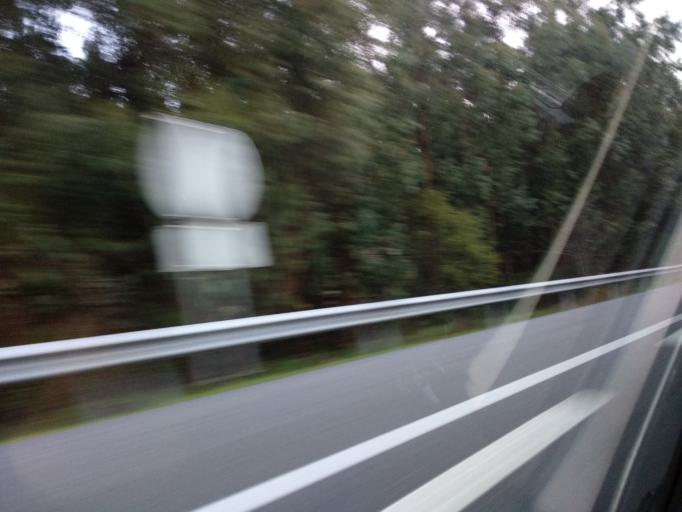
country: PT
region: Braga
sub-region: Braga
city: Oliveira
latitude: 41.4563
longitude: -8.4843
